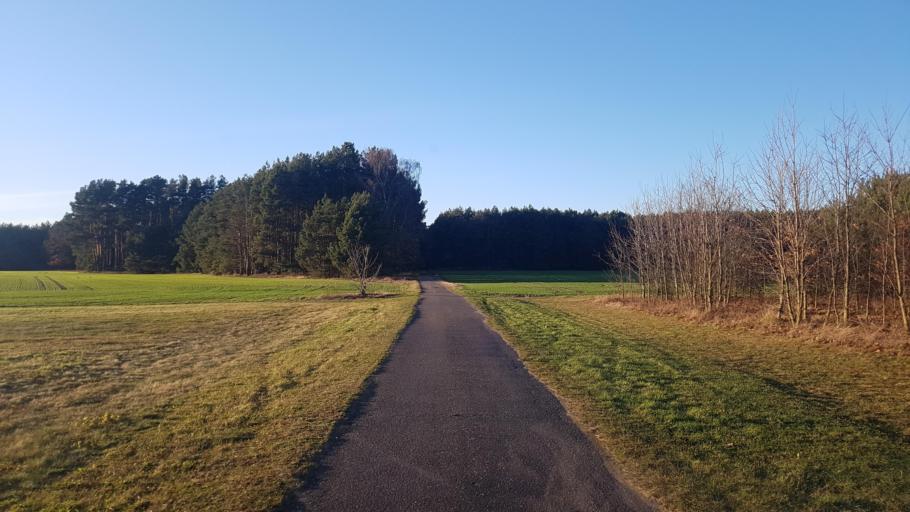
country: DE
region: Brandenburg
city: Drehnow
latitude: 51.8881
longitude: 14.3932
